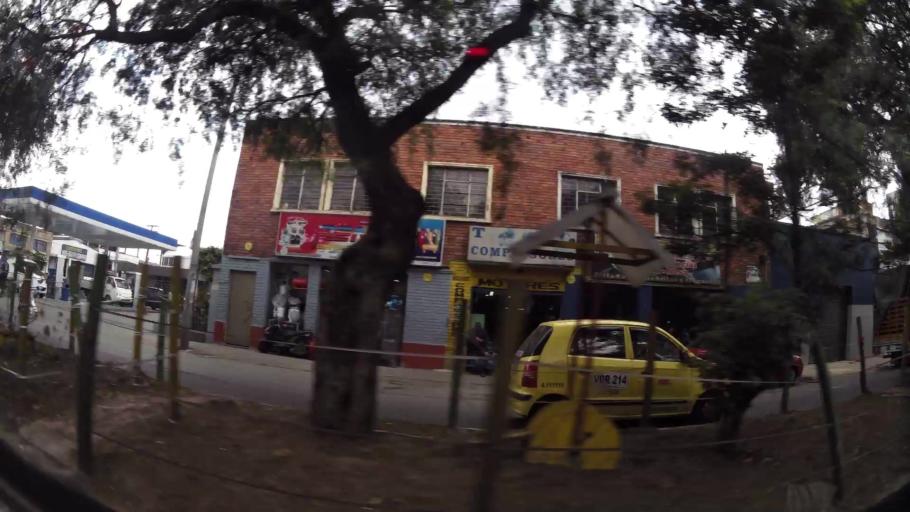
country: CO
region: Bogota D.C.
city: Bogota
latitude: 4.6044
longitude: -74.0922
